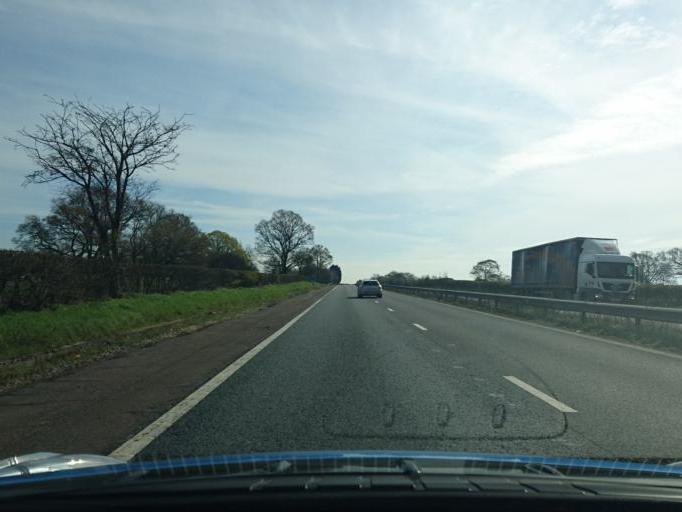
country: GB
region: England
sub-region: Herefordshire
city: Donnington
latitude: 51.9951
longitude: -2.3305
